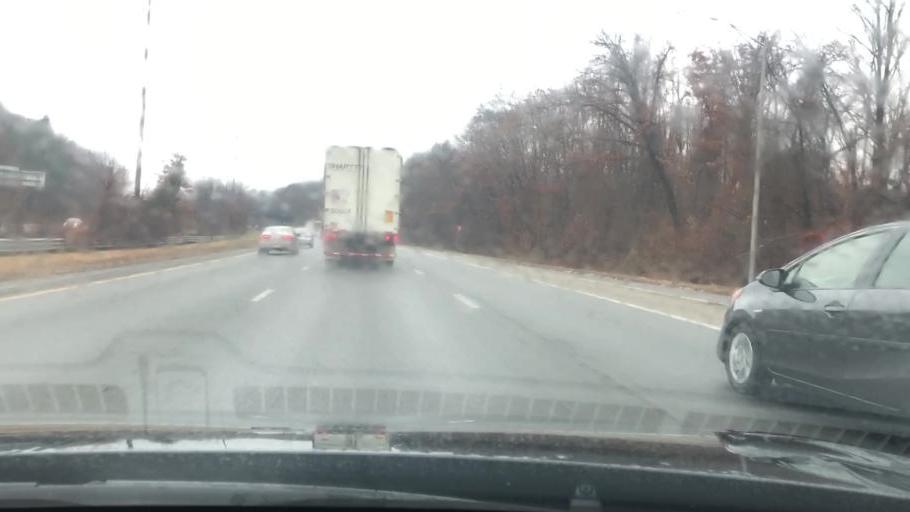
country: US
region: Massachusetts
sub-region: Middlesex County
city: Chelmsford
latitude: 42.6025
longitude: -71.3570
